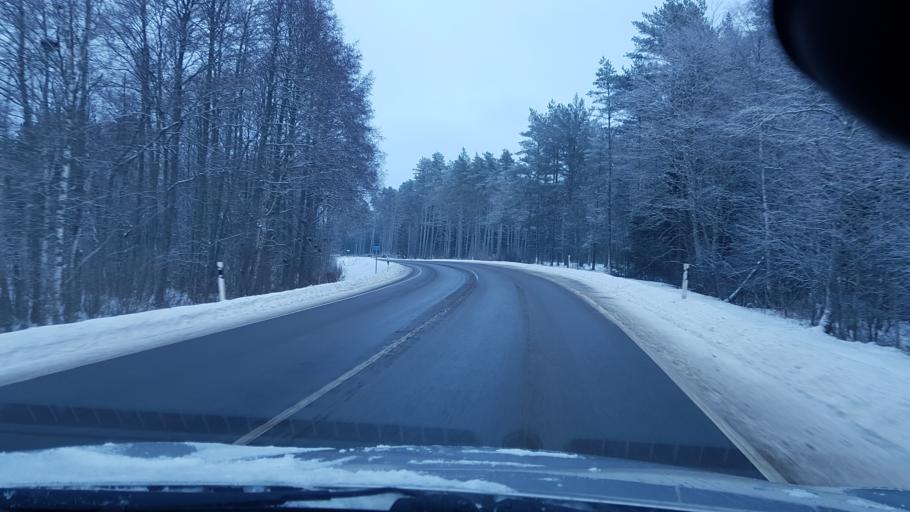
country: EE
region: Harju
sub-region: Keila linn
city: Keila
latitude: 59.3370
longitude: 24.2492
